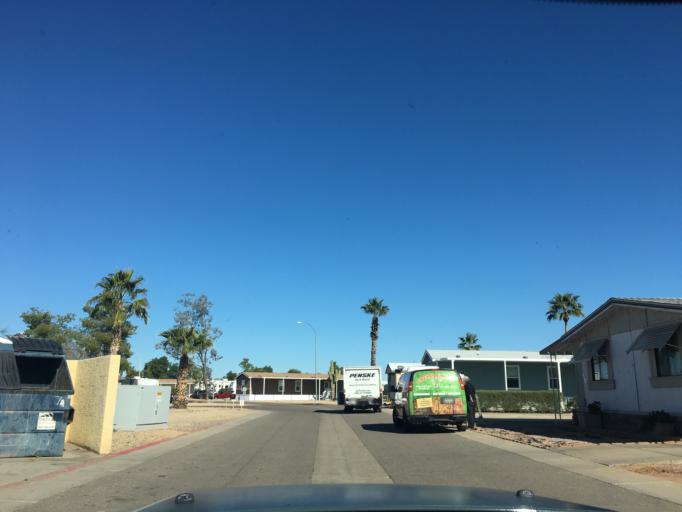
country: US
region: Arizona
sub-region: Maricopa County
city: Mesa
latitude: 33.4486
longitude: -111.8437
